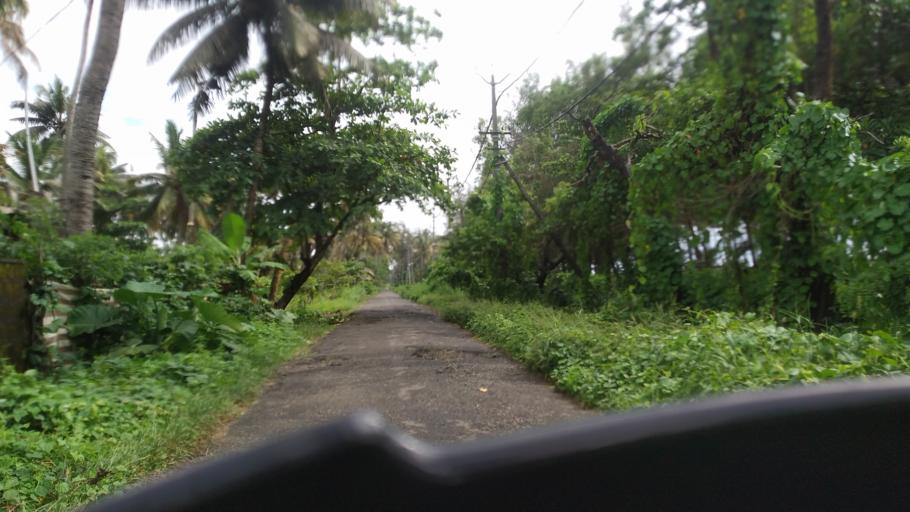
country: IN
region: Kerala
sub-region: Thrissur District
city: Kodungallur
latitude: 10.1196
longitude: 76.1852
